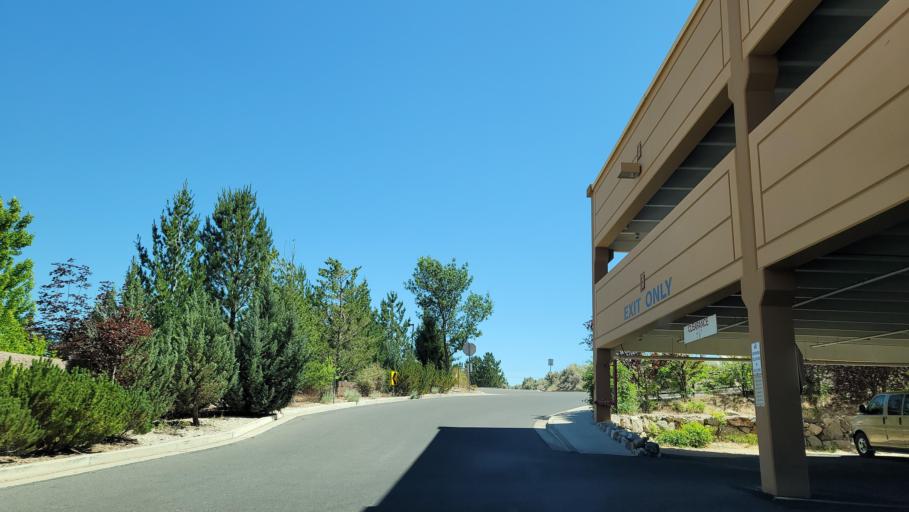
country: US
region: Nevada
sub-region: Carson City
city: Carson City
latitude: 39.1307
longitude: -119.7715
